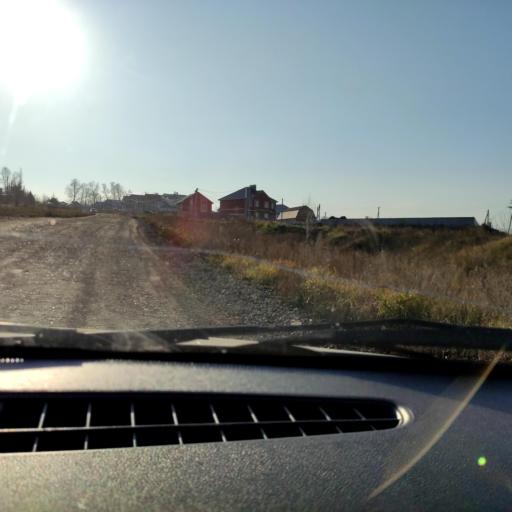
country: RU
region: Bashkortostan
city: Kabakovo
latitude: 54.6336
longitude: 56.0728
